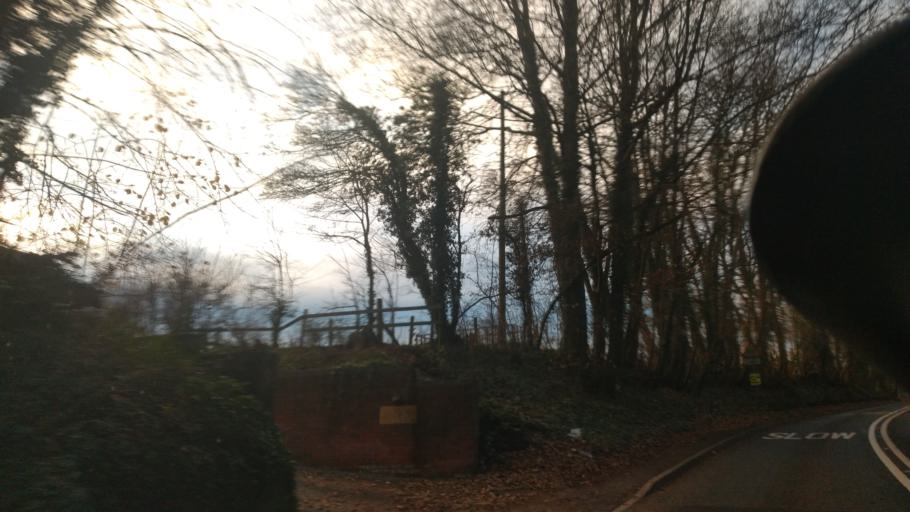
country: GB
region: England
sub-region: Somerset
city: Frome
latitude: 51.2461
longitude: -2.3100
